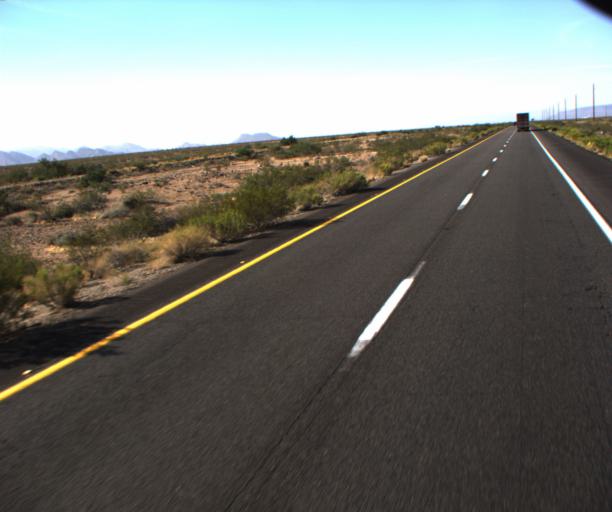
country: US
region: Arizona
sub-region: Mohave County
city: Kingman
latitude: 35.0616
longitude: -114.1256
